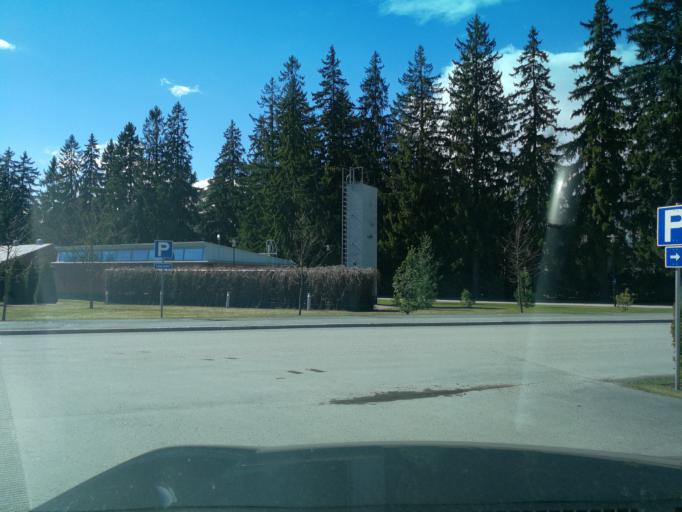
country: FI
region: Uusimaa
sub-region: Helsinki
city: Vantaa
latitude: 60.2403
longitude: 25.0263
